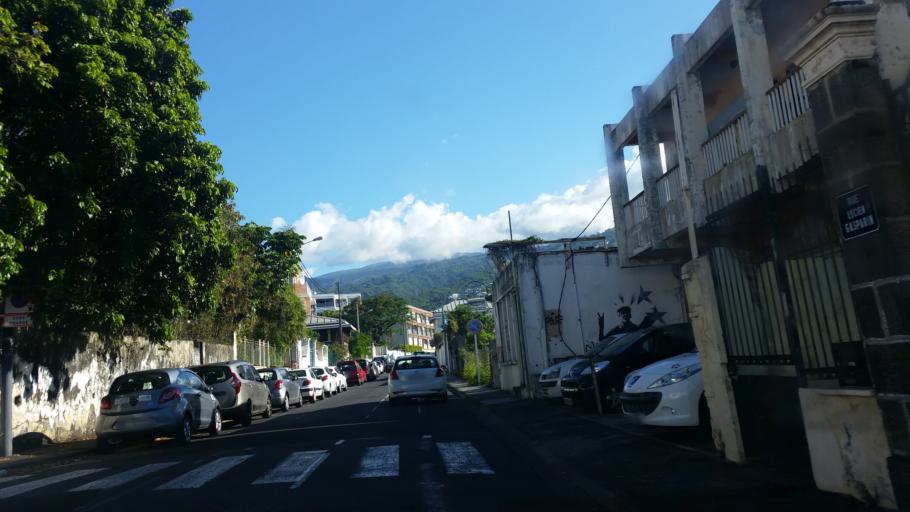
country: RE
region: Reunion
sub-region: Reunion
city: Saint-Denis
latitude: -20.8819
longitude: 55.4475
